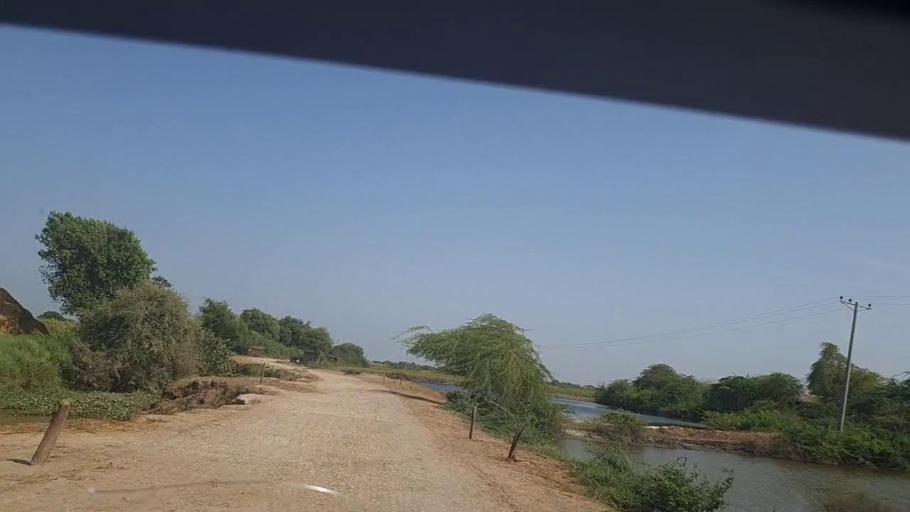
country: PK
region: Sindh
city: Rajo Khanani
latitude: 24.9678
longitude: 68.8816
